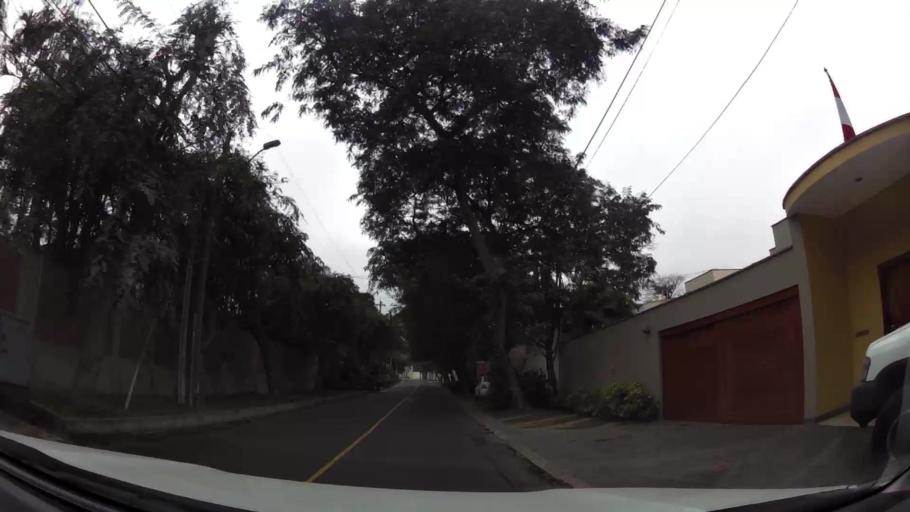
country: PE
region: Lima
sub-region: Lima
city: La Molina
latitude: -12.0751
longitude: -76.9151
